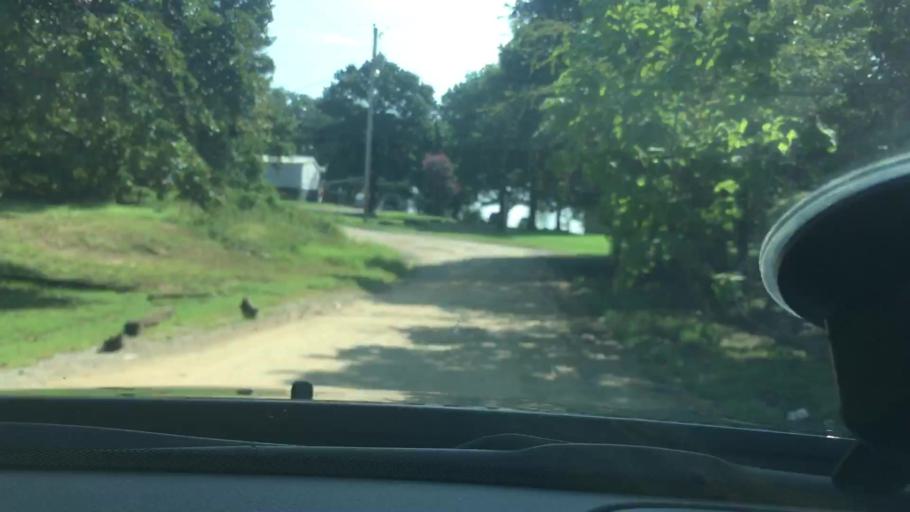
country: US
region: Texas
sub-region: Grayson County
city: Preston
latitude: 33.8906
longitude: -96.5632
